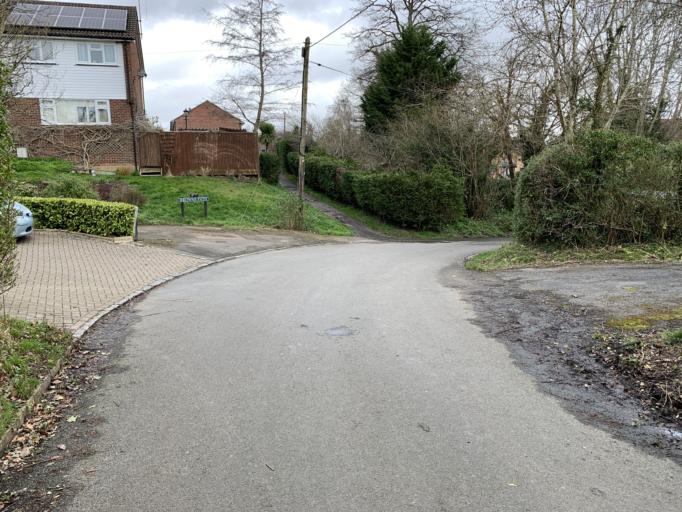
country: GB
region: England
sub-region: East Sussex
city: Uckfield
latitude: 50.9763
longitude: 0.1094
